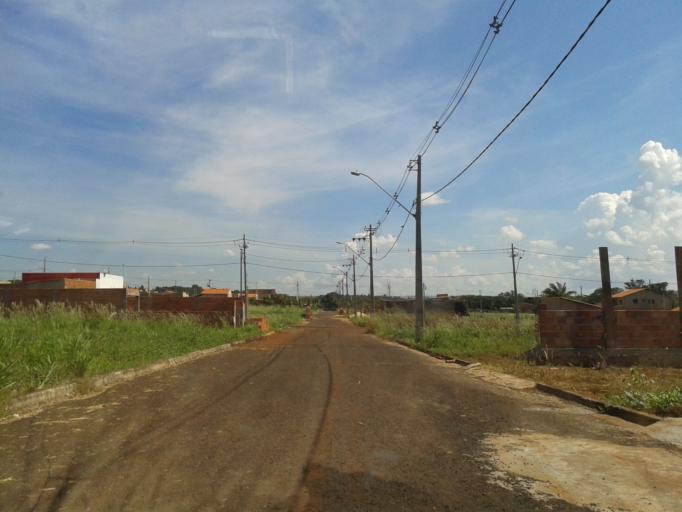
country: BR
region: Goias
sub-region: Itumbiara
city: Itumbiara
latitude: -18.4226
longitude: -49.1815
